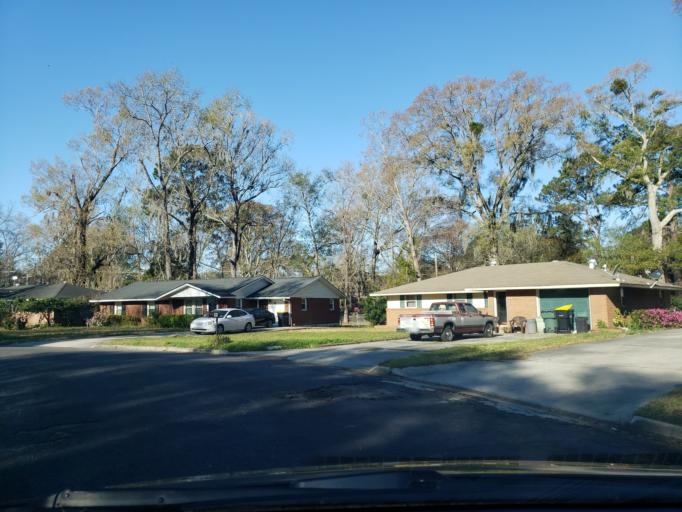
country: US
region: Georgia
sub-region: Chatham County
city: Montgomery
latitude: 31.9860
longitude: -81.1360
